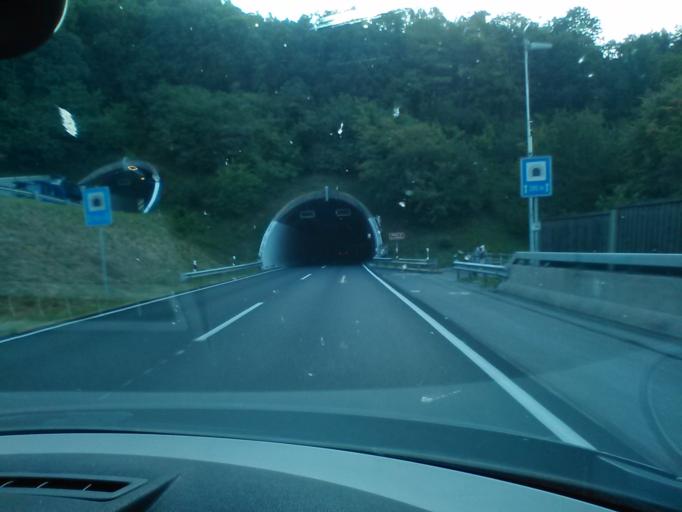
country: CH
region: Vaud
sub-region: Lavaux-Oron District
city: Cully
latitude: 46.4992
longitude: 6.7262
